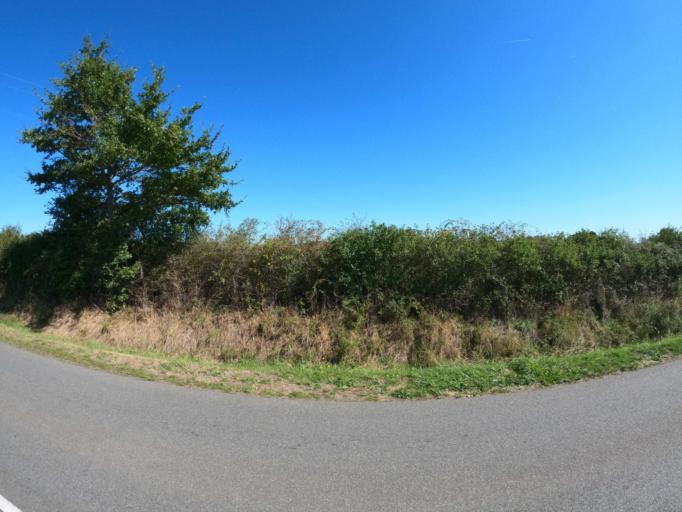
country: FR
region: Limousin
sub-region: Departement de la Haute-Vienne
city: Le Dorat
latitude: 46.2410
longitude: 1.0535
